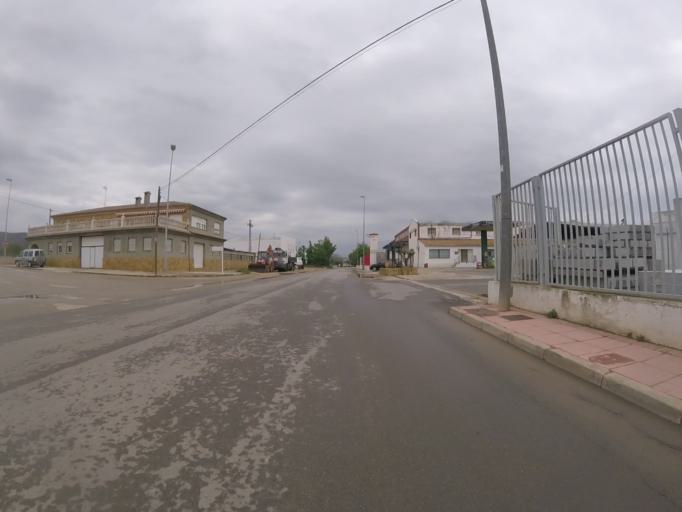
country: ES
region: Valencia
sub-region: Provincia de Castello
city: Alcala de Xivert
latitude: 40.3090
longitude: 0.2291
